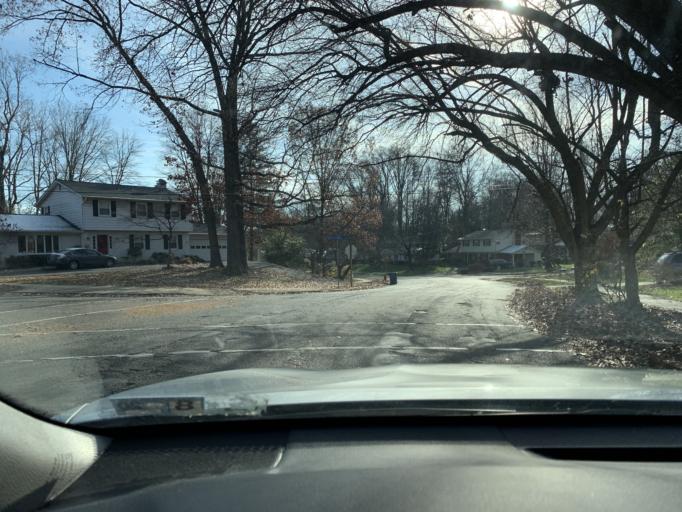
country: US
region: Virginia
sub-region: Fairfax County
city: Jefferson
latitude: 38.8531
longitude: -77.1833
